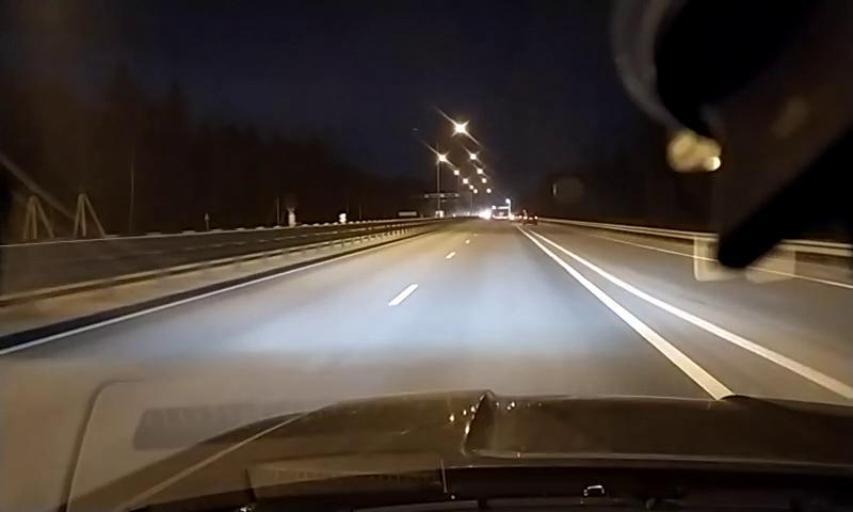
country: RU
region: Leningrad
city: Agalatovo
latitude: 60.2203
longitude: 30.3589
